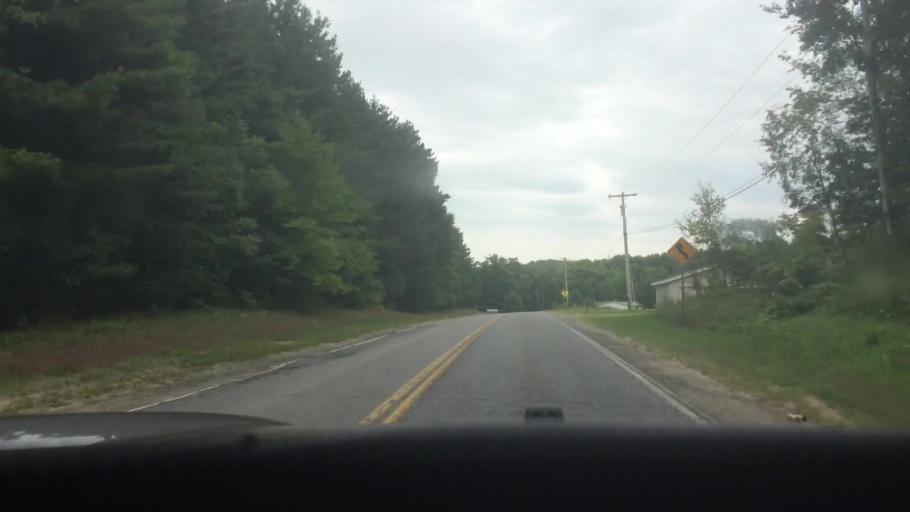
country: US
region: New York
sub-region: St. Lawrence County
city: Hannawa Falls
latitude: 44.6105
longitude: -74.8816
